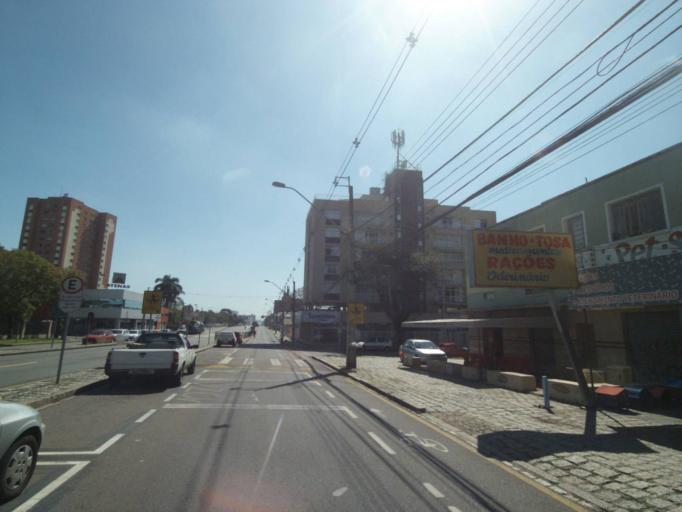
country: BR
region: Parana
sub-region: Curitiba
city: Curitiba
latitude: -25.3972
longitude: -49.2439
